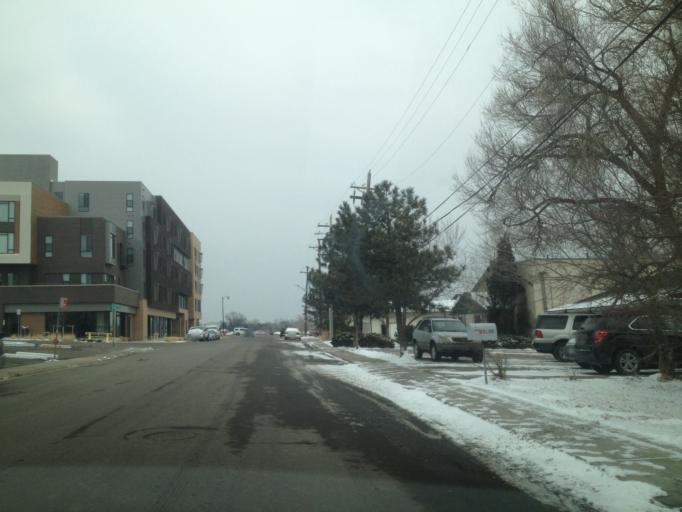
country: US
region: Colorado
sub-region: Adams County
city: Westminster
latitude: 39.8246
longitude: -105.0270
